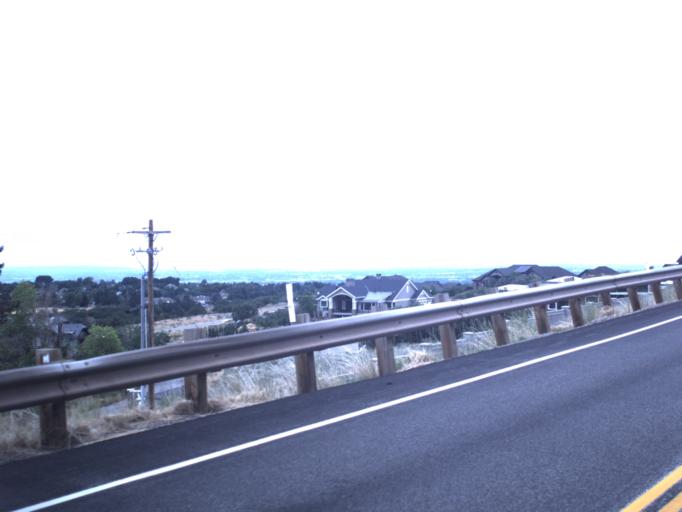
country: US
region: Utah
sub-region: Salt Lake County
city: Granite
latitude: 40.5793
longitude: -111.7911
